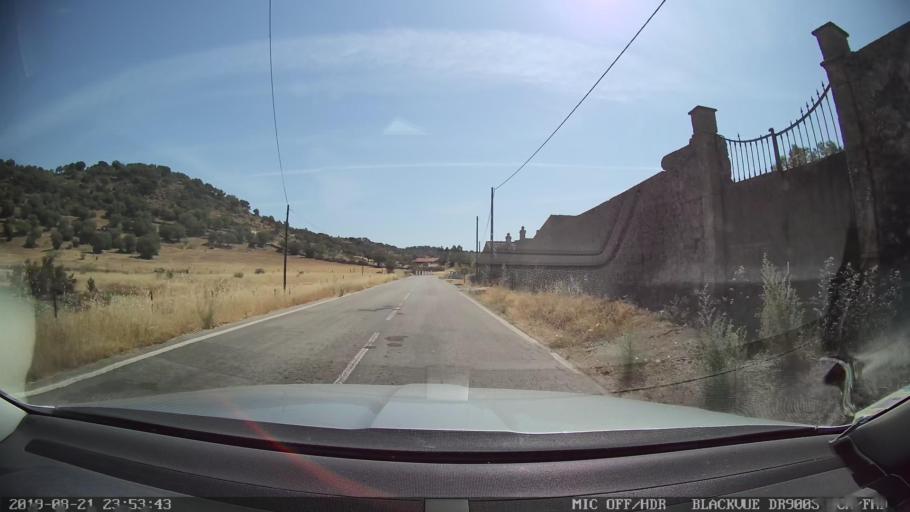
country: PT
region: Castelo Branco
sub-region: Idanha-A-Nova
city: Idanha-a-Nova
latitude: 39.9091
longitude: -7.2130
